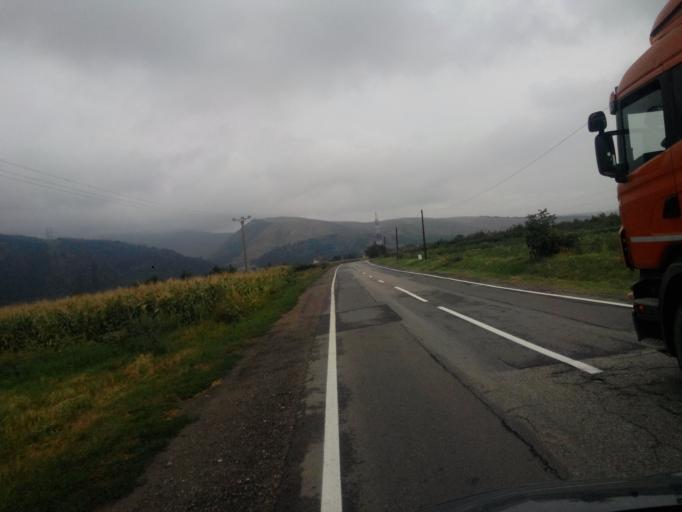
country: RO
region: Cluj
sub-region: Comuna Moldovenesti
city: Moldovenesti
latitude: 46.5137
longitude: 23.6793
